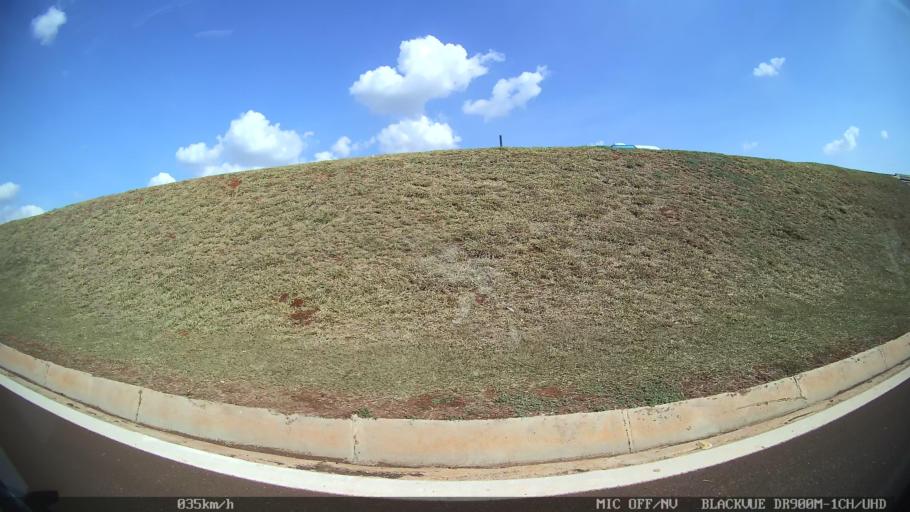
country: BR
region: Sao Paulo
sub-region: Ribeirao Preto
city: Ribeirao Preto
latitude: -21.2048
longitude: -47.8609
